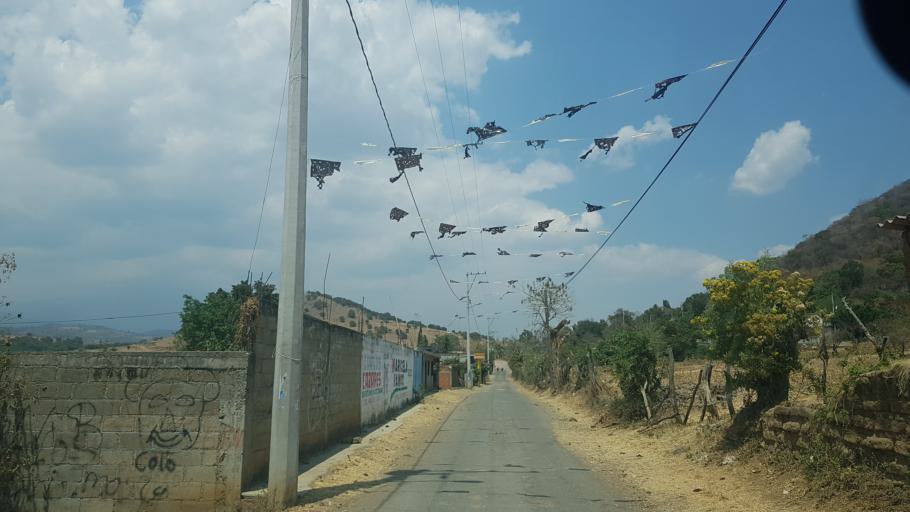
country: MX
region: Puebla
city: San Juan Amecac
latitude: 18.8062
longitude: -98.6239
